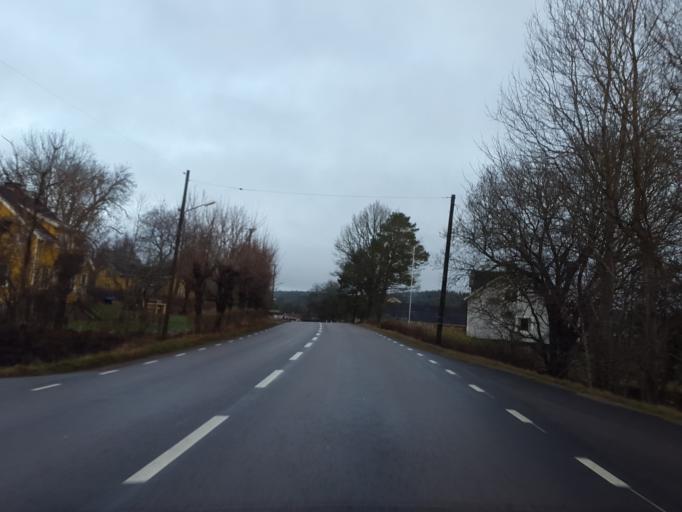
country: SE
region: Vaestra Goetaland
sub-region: Boras Kommun
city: Sandared
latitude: 57.8052
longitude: 12.7544
